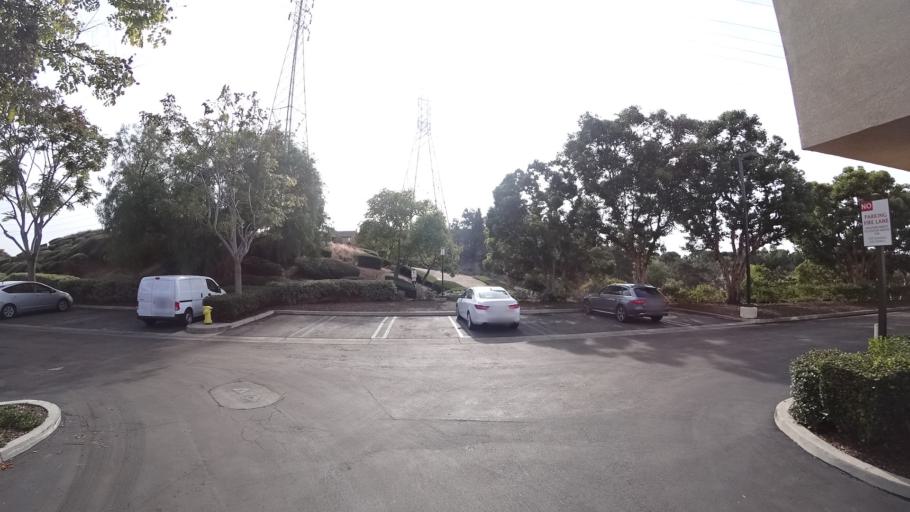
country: US
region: California
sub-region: Orange County
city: Laguna Woods
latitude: 33.5951
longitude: -117.7354
